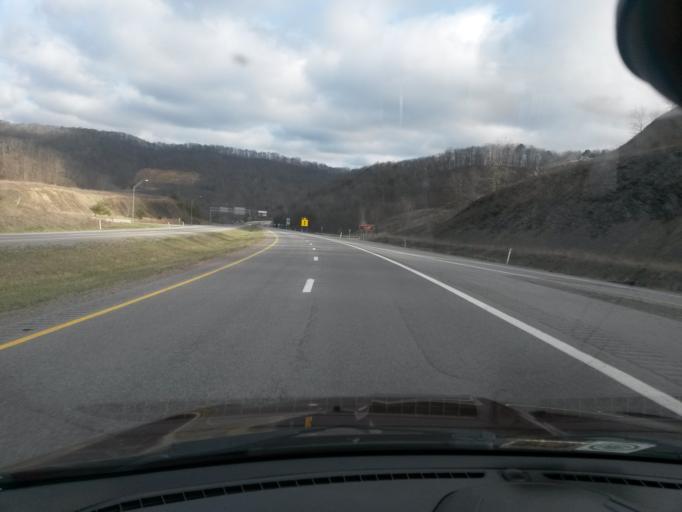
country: US
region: West Virginia
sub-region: Mercer County
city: Bluefield
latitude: 37.2770
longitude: -81.1638
